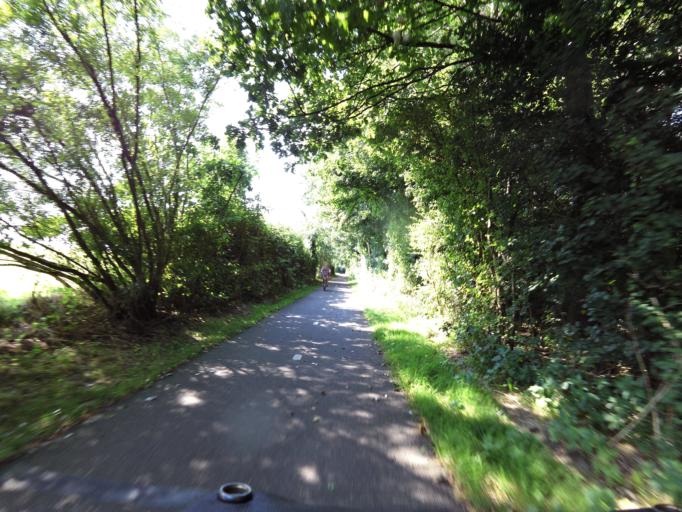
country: NL
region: South Holland
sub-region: Gemeente Barendrecht
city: Barendrecht
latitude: 51.8252
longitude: 4.5239
